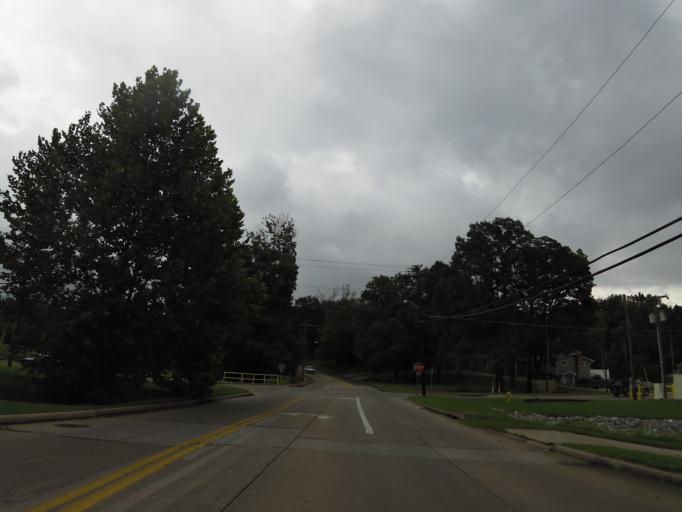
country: US
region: Missouri
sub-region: Cape Girardeau County
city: Cape Girardeau
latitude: 37.3285
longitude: -89.5444
